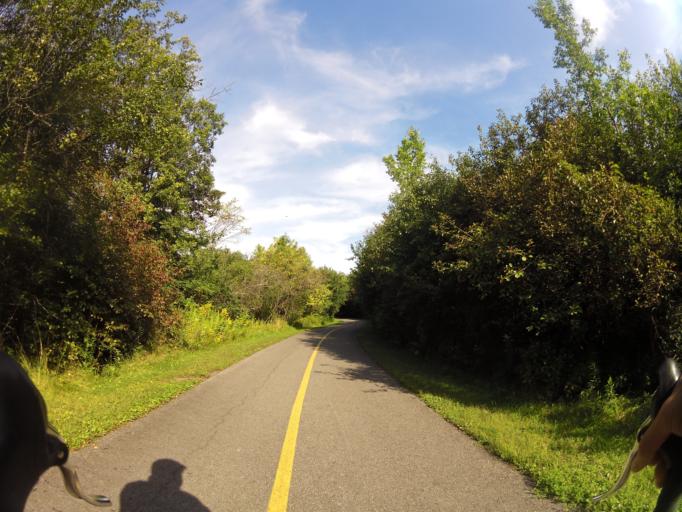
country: CA
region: Ontario
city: Bells Corners
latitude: 45.3422
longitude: -75.8747
